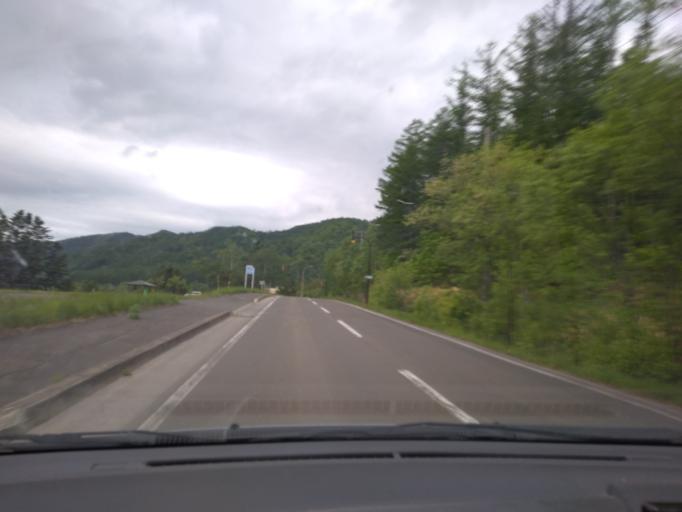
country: JP
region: Hokkaido
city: Shimo-furano
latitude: 43.1604
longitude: 142.4963
